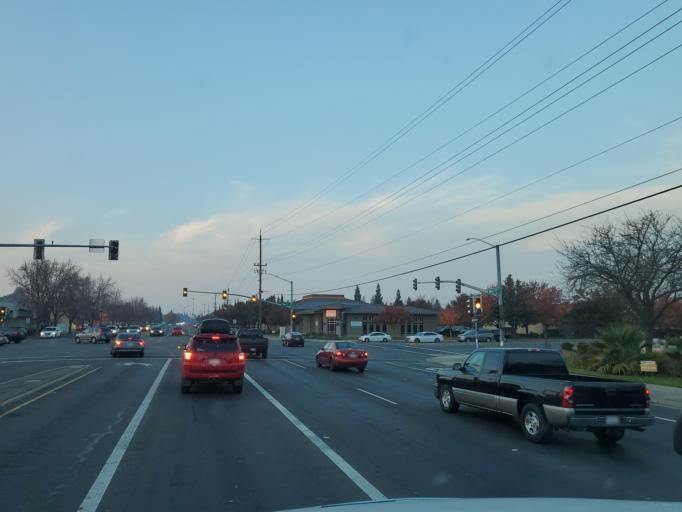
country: US
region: California
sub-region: San Joaquin County
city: August
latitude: 38.0016
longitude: -121.2905
